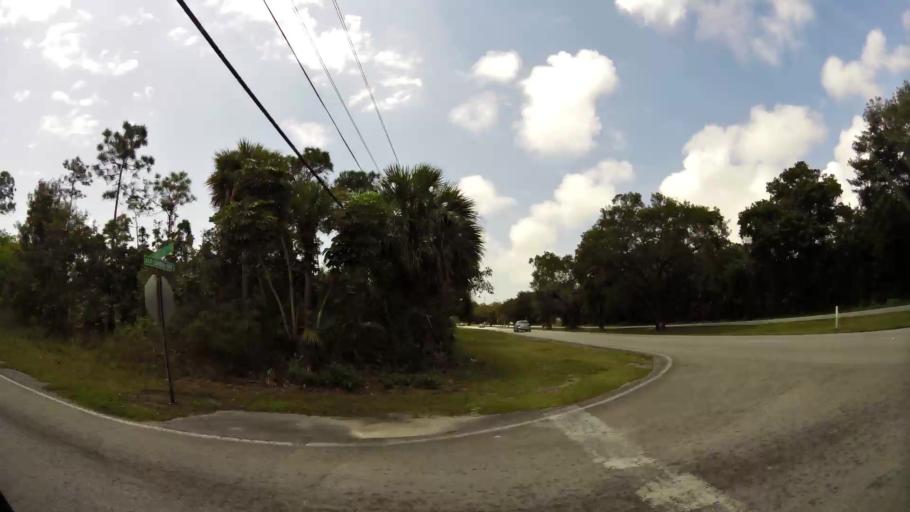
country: BS
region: Freeport
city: Lucaya
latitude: 26.5255
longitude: -78.6576
